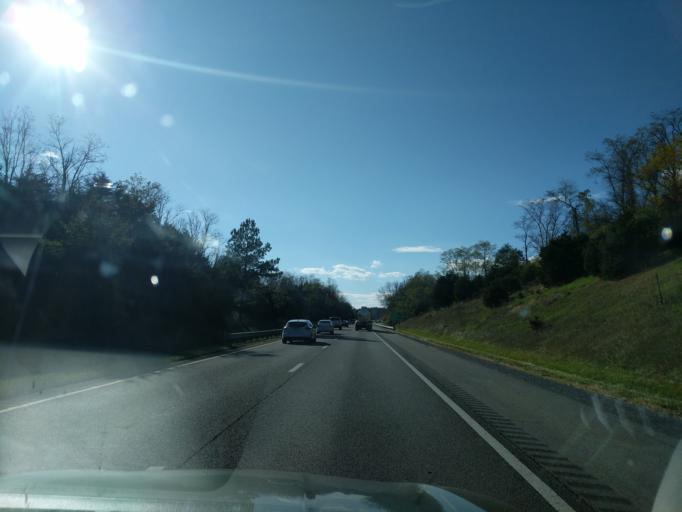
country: US
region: Virginia
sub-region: Pulaski County
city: Dublin
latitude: 37.0810
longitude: -80.6603
